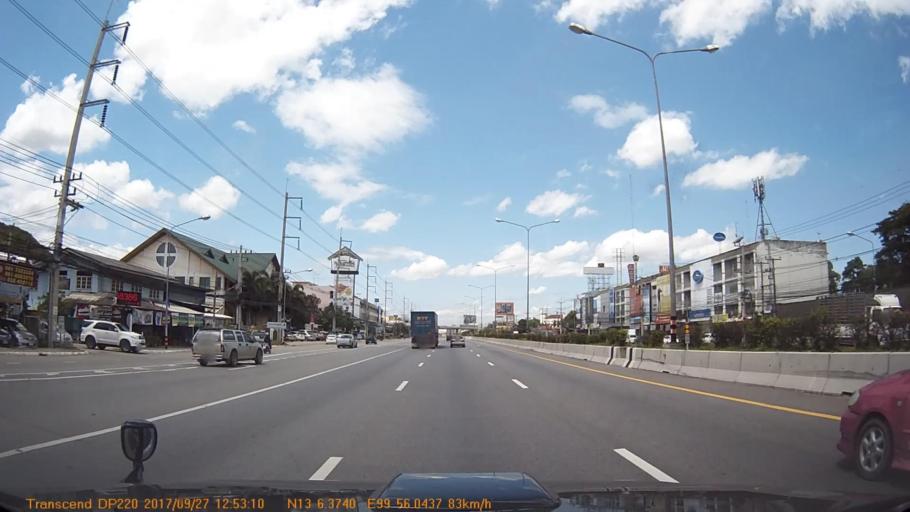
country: TH
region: Phetchaburi
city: Phetchaburi
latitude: 13.1067
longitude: 99.9339
